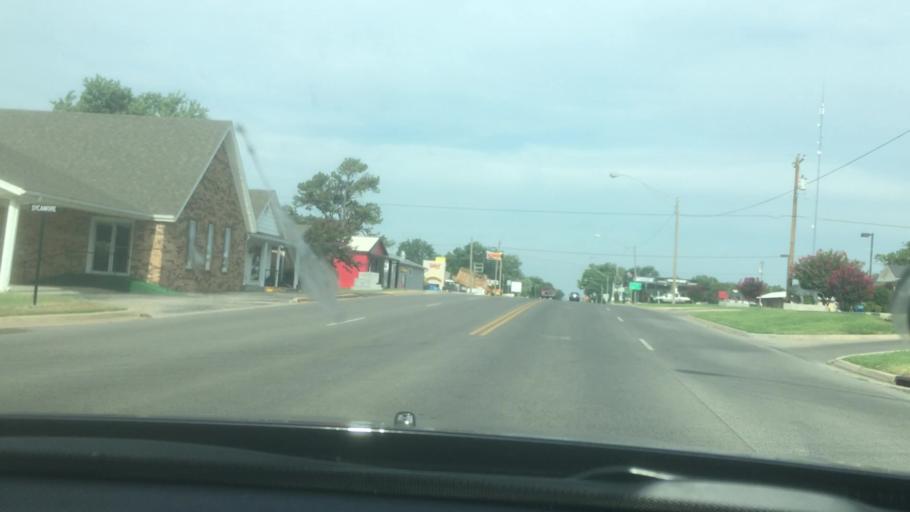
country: US
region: Oklahoma
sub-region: Garvin County
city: Stratford
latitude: 34.7967
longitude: -96.9647
